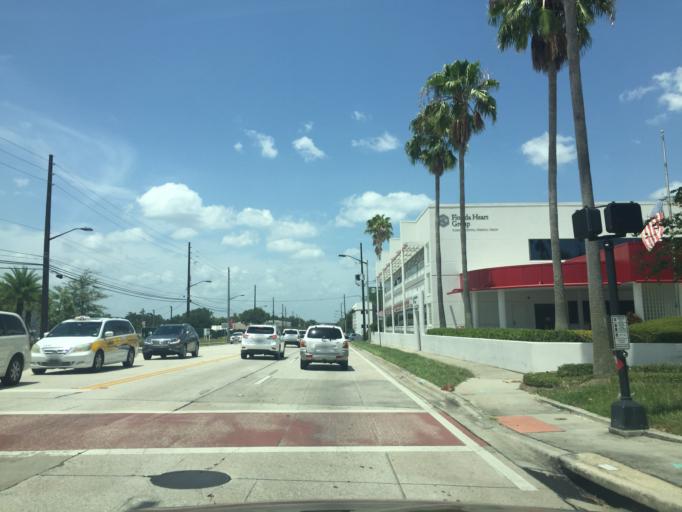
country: US
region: Florida
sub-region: Orange County
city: Orlando
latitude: 28.5656
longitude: -81.3644
